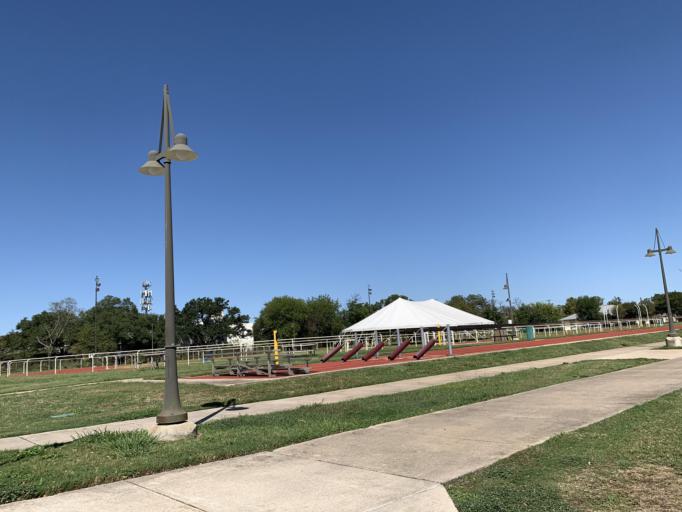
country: US
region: Texas
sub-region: Travis County
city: Austin
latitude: 30.3166
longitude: -97.7373
